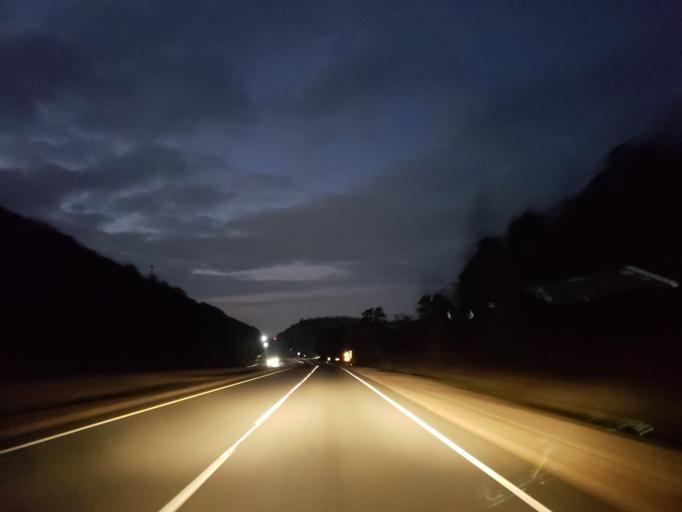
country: US
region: Georgia
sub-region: Polk County
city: Rockmart
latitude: 33.9722
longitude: -85.0019
